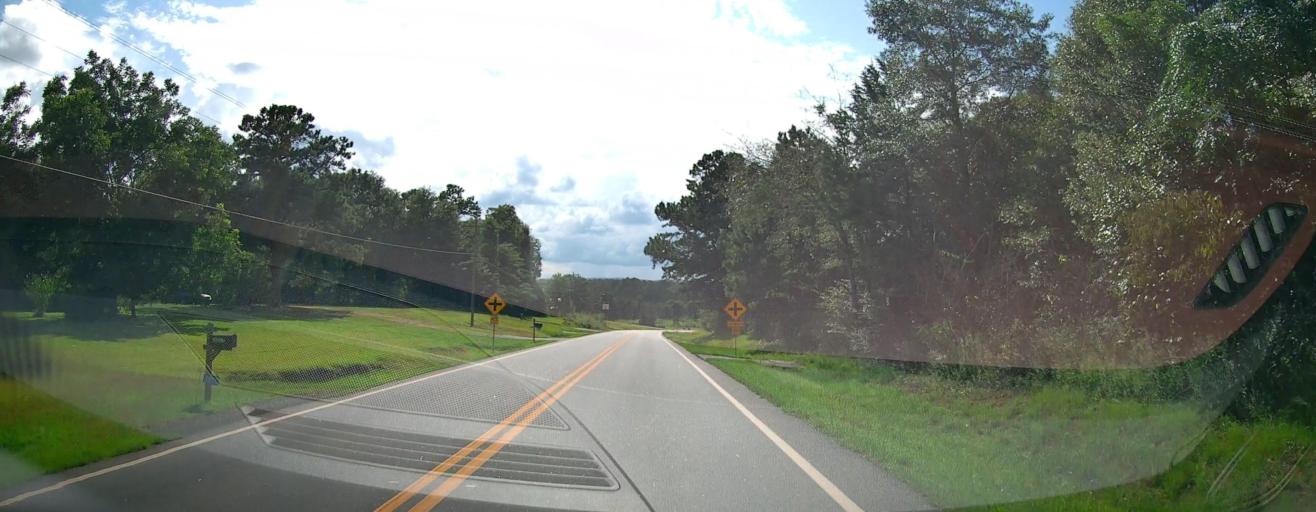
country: US
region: Georgia
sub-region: Upson County
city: Hannahs Mill
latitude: 32.8985
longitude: -84.4095
